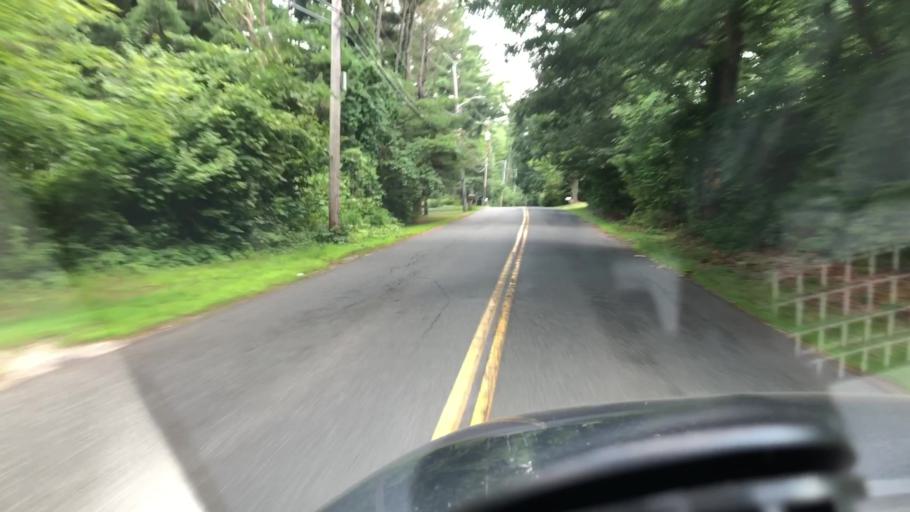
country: US
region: Massachusetts
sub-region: Hampden County
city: Holyoke
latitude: 42.1878
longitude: -72.6773
